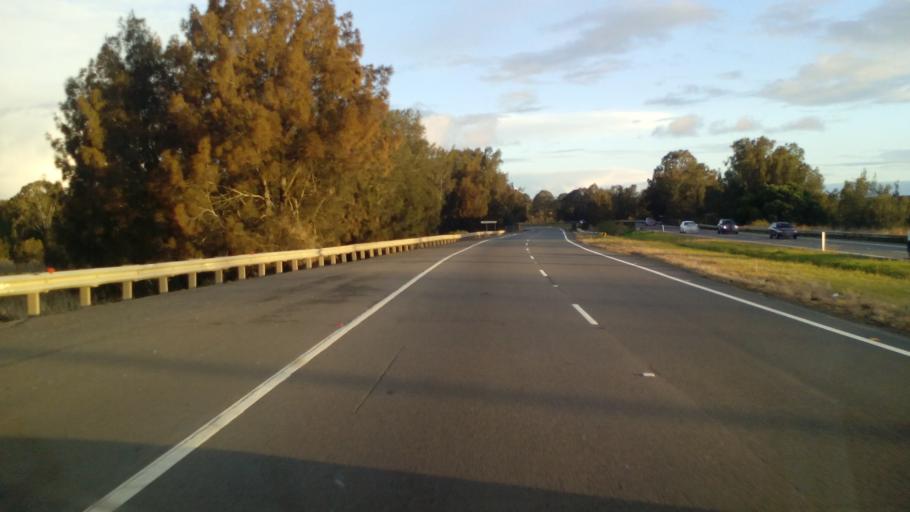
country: AU
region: New South Wales
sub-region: Newcastle
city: Beresfield
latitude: -32.7993
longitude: 151.6396
